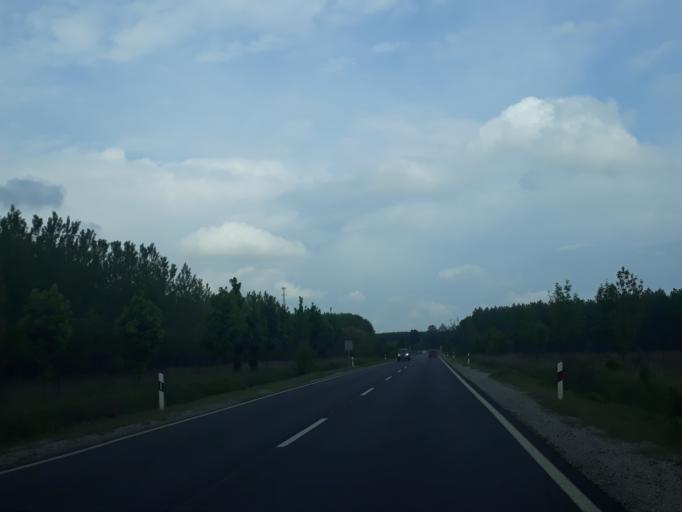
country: HU
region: Szabolcs-Szatmar-Bereg
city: Nyirbogdany
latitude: 48.0438
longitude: 21.8741
